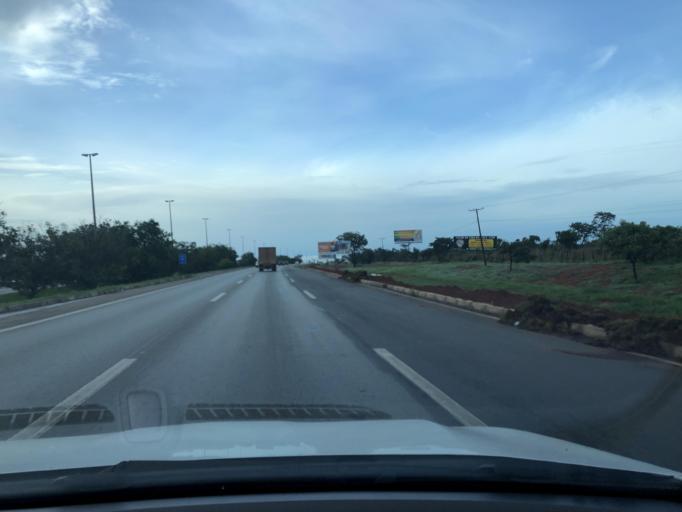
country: BR
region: Goias
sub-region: Luziania
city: Luziania
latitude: -16.0291
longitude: -47.9789
